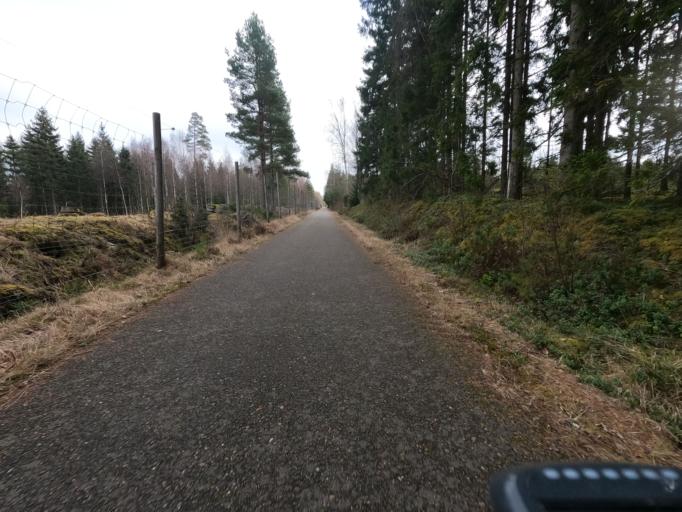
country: SE
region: Joenkoeping
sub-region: Varnamo Kommun
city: Rydaholm
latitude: 56.8578
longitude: 14.1799
